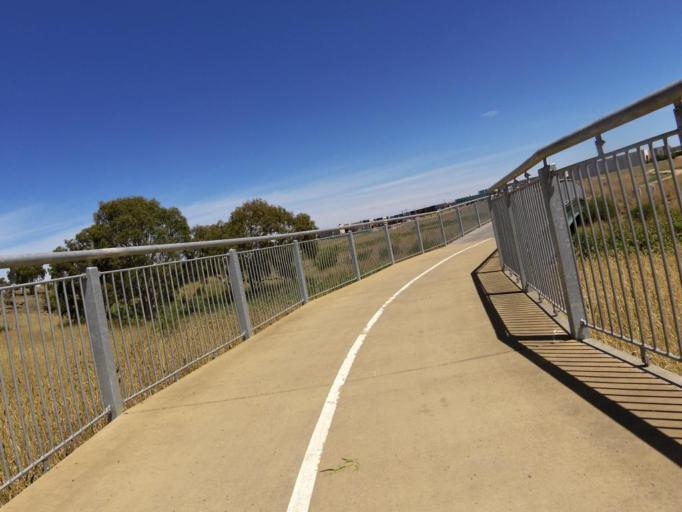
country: AU
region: Victoria
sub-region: Hume
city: Campbellfield
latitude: -37.6669
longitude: 144.9763
